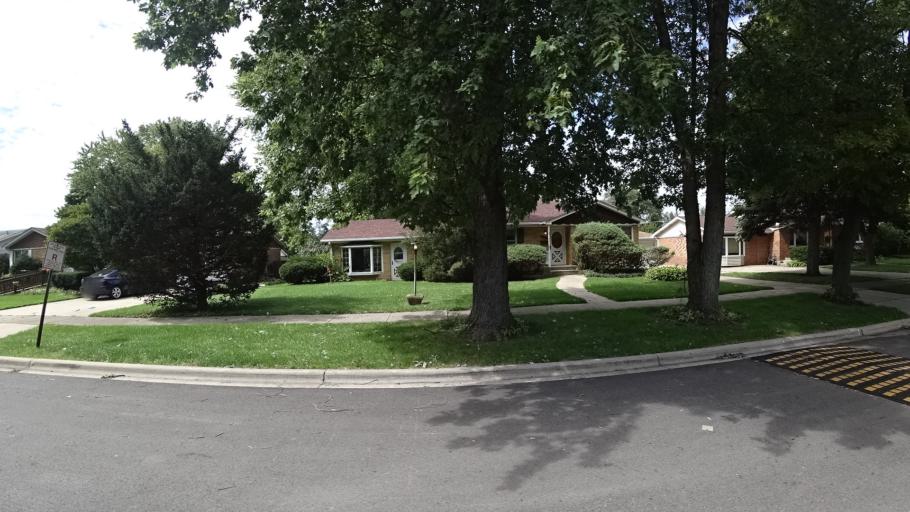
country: US
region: Illinois
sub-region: Cook County
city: Chicago Ridge
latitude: 41.7038
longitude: -87.7858
